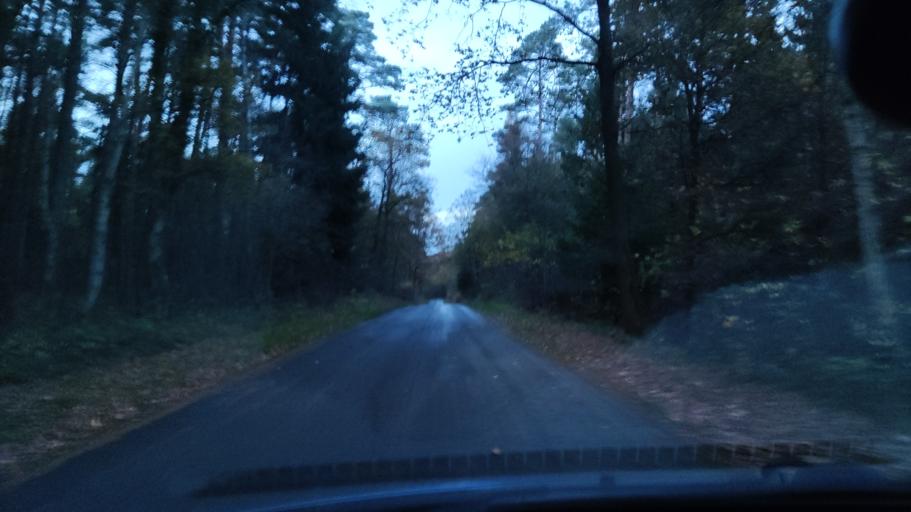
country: DE
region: Lower Saxony
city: Egestorf
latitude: 53.1548
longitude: 10.0345
